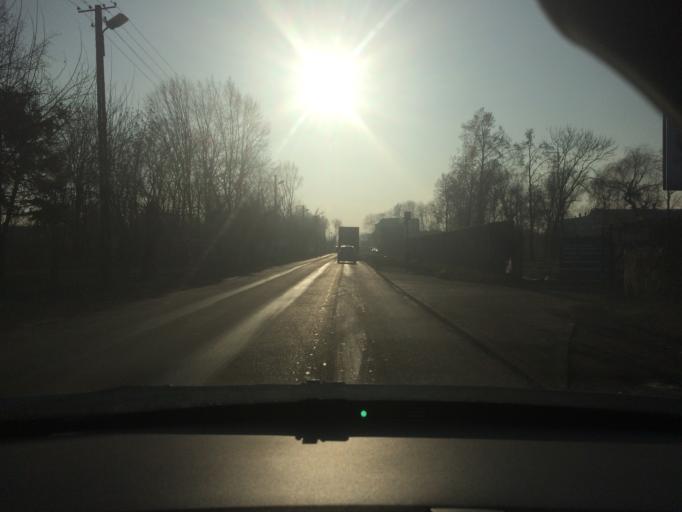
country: PL
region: Lesser Poland Voivodeship
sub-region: Powiat wielicki
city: Czarnochowice
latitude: 50.0281
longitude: 20.0393
